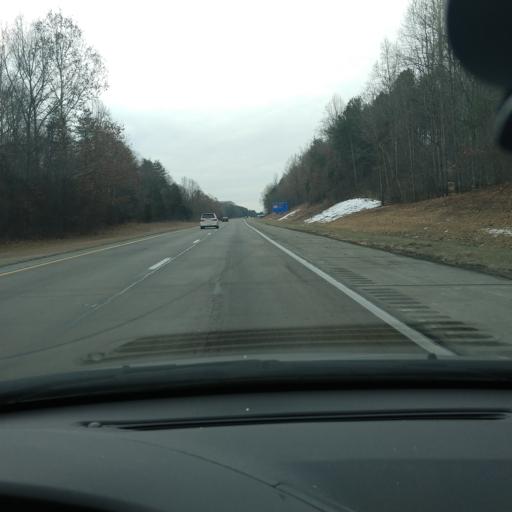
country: US
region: North Carolina
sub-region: Davidson County
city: Midway
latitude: 35.9799
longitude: -80.2334
